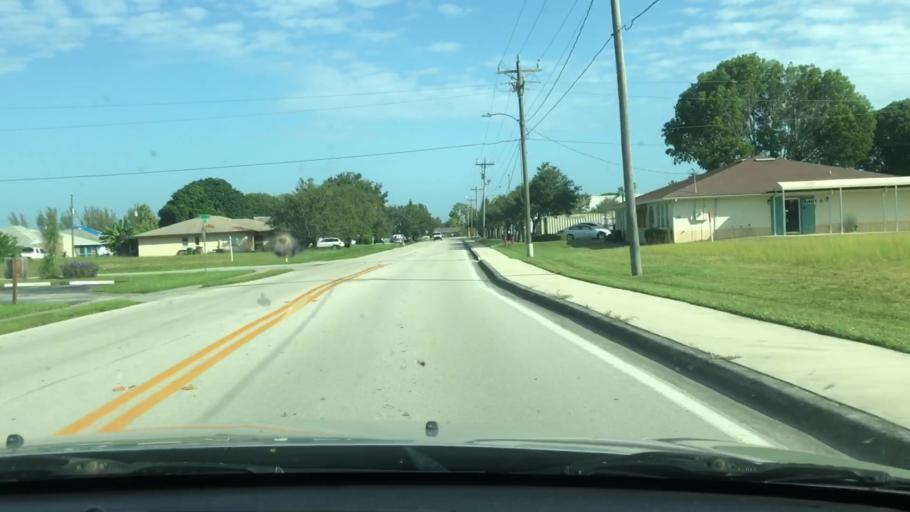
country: US
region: Florida
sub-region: Lee County
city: Lochmoor Waterway Estates
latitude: 26.6385
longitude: -81.9456
